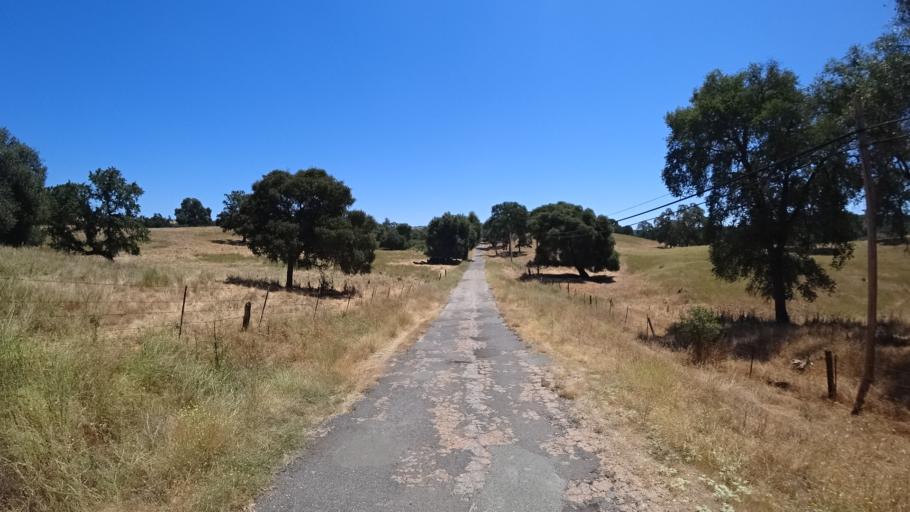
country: US
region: California
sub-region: Calaveras County
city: Angels Camp
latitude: 38.1112
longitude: -120.6167
